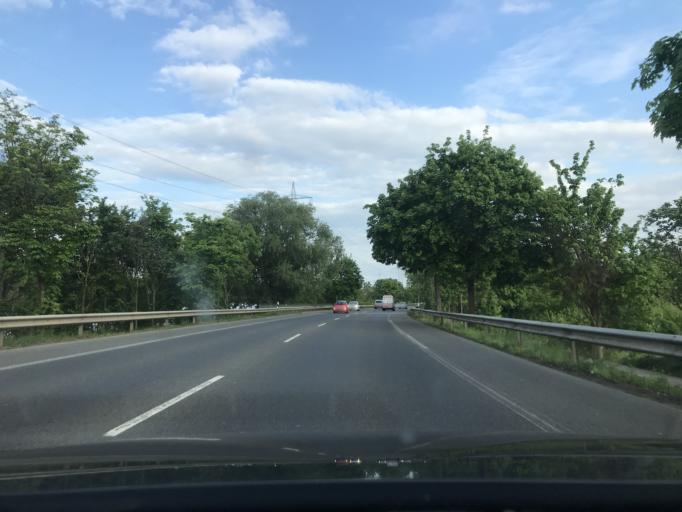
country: DE
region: North Rhine-Westphalia
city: Bornheim
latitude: 50.7774
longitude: 6.9939
